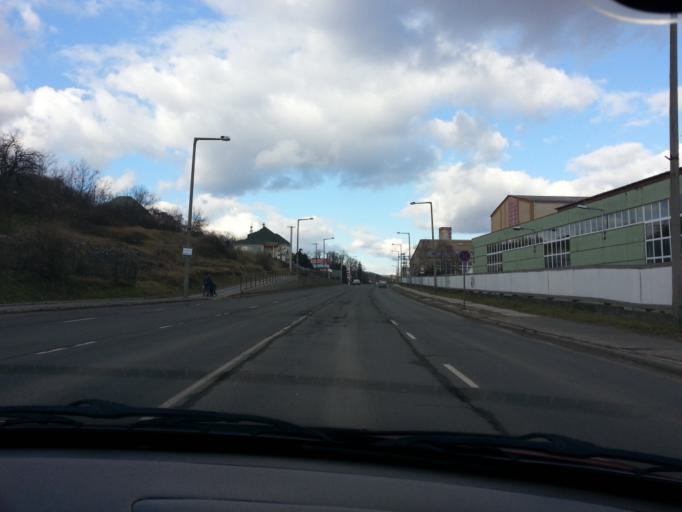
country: HU
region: Nograd
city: Salgotarjan
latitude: 48.0676
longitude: 19.7832
